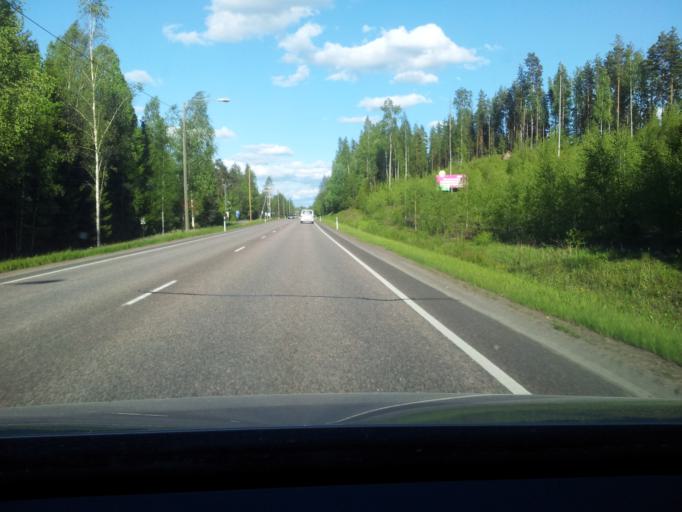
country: FI
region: Kymenlaakso
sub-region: Kouvola
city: Kouvola
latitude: 60.8862
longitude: 26.8159
